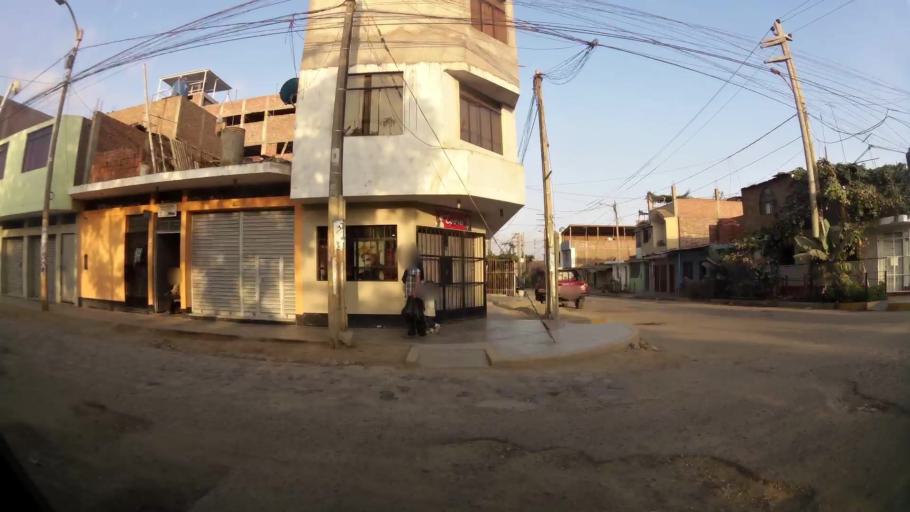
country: PE
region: La Libertad
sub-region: Provincia de Trujillo
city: El Porvenir
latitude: -8.0763
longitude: -78.9957
